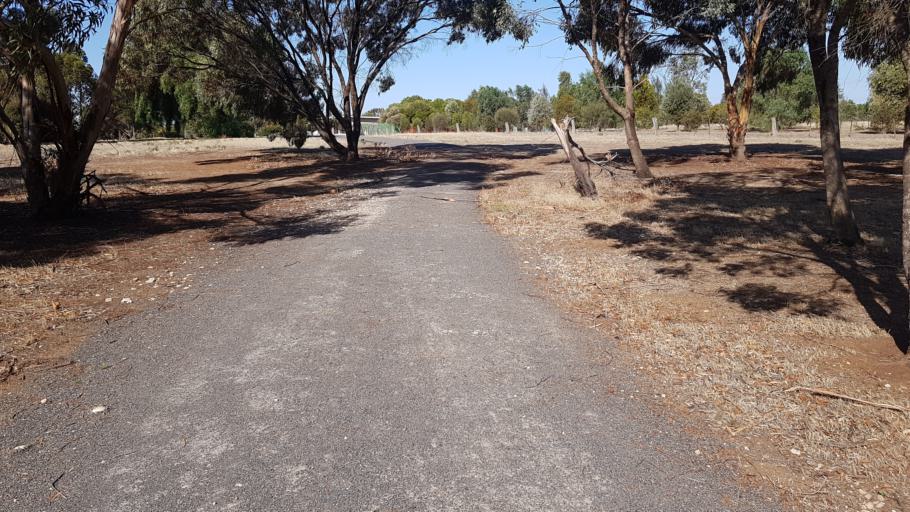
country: AU
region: Victoria
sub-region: Horsham
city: Horsham
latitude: -36.7460
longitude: 141.9382
